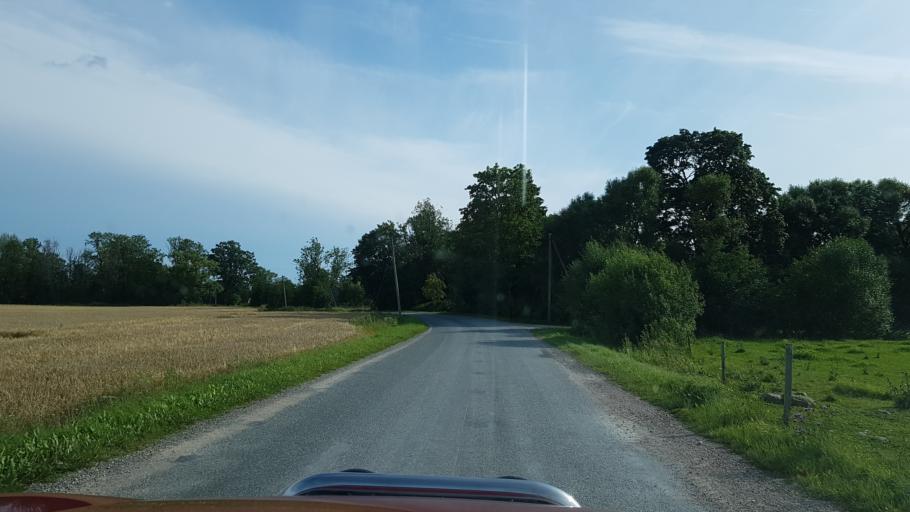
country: EE
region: Laeaene
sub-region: Lihula vald
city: Lihula
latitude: 58.4520
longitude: 23.9960
